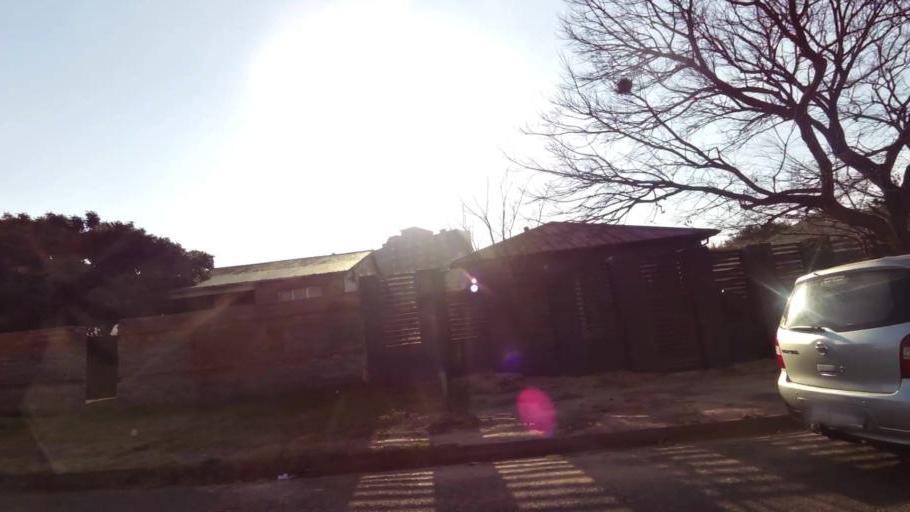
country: ZA
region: Gauteng
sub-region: City of Johannesburg Metropolitan Municipality
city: Johannesburg
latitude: -26.1918
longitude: 28.0149
